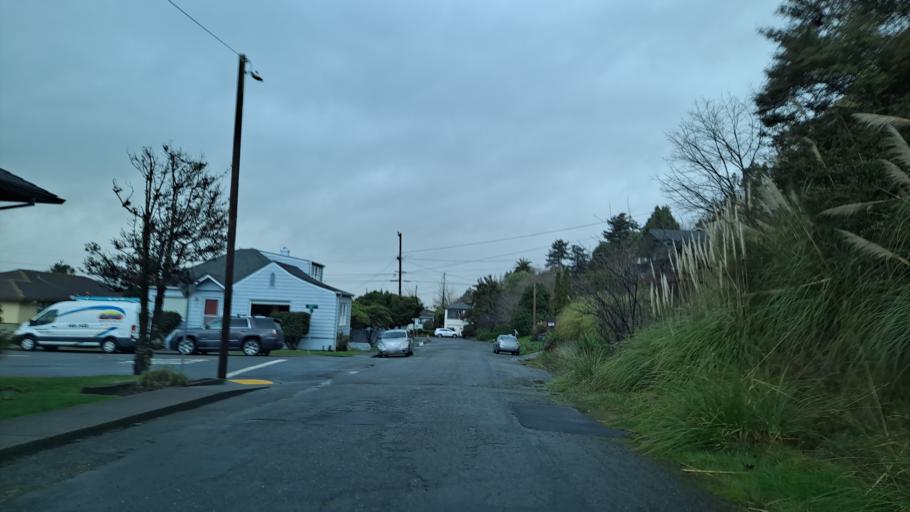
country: US
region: California
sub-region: Humboldt County
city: Fortuna
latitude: 40.6003
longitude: -124.1531
